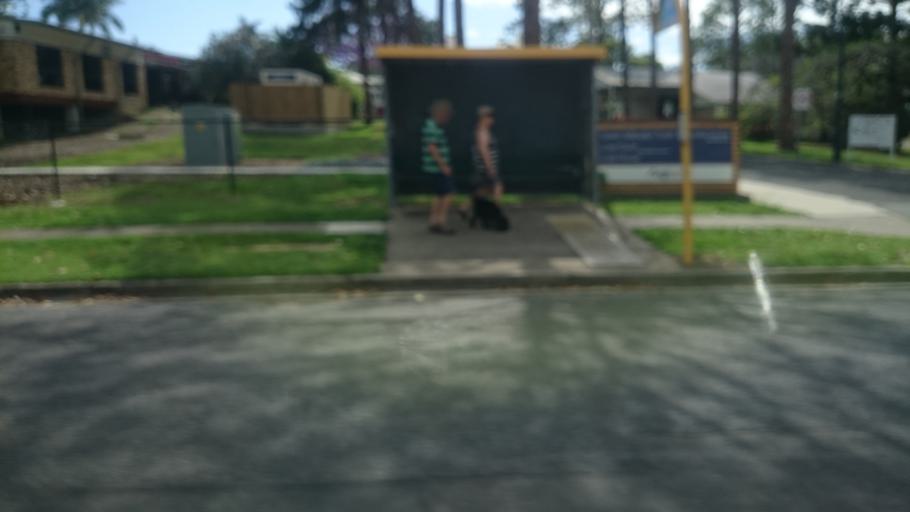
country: AU
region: Queensland
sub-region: Brisbane
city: Manly West
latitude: -27.4632
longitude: 153.1882
